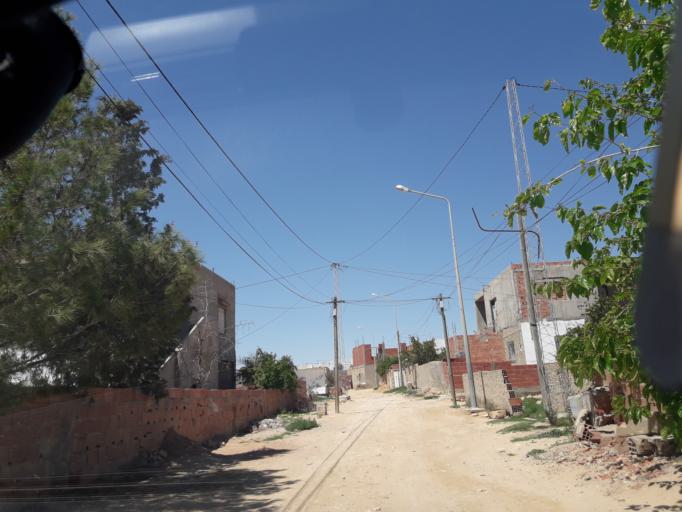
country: TN
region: Safaqis
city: Sfax
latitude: 34.7415
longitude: 10.5194
